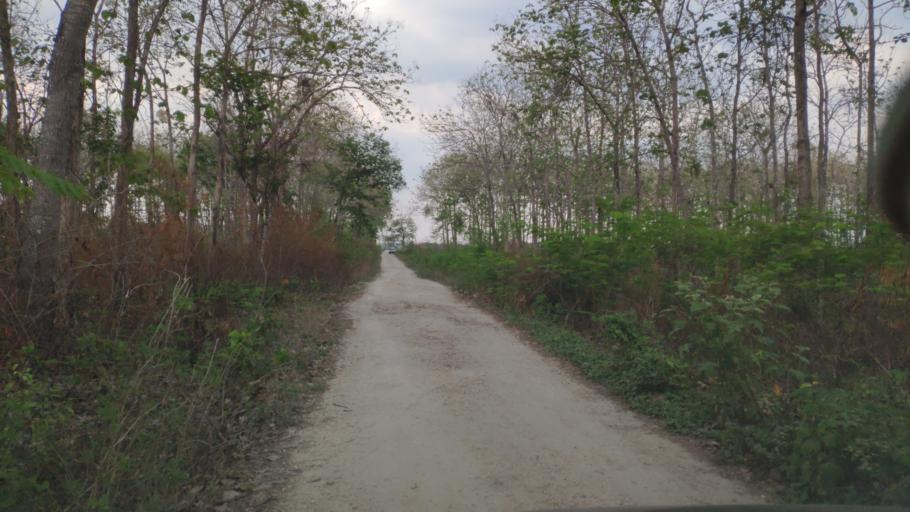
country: ID
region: Central Java
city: Randublatung
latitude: -7.2873
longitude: 111.2960
